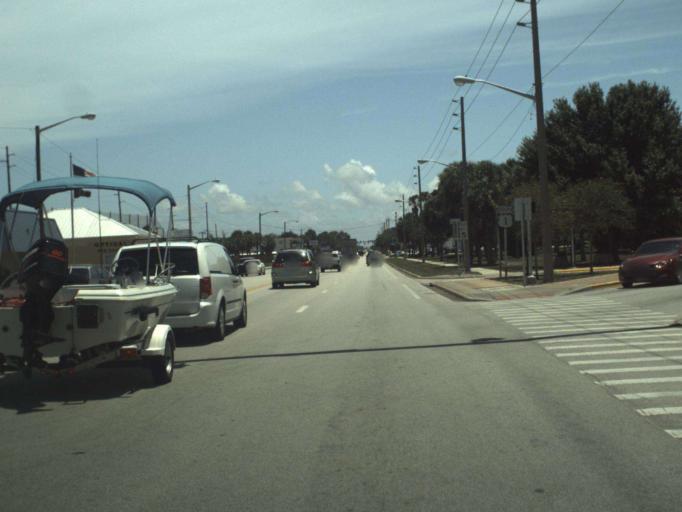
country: US
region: Florida
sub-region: Saint Lucie County
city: Fort Pierce
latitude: 27.4396
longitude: -80.3260
